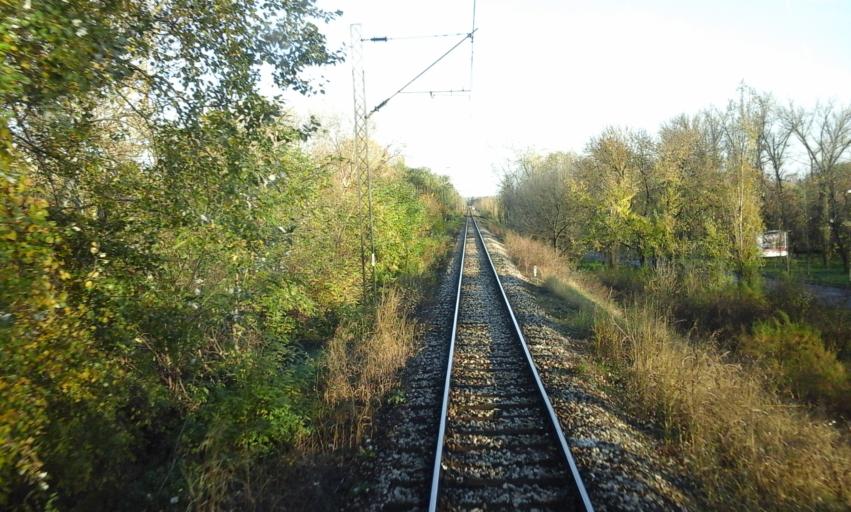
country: RS
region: Autonomna Pokrajina Vojvodina
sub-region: Juznobacki Okrug
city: Petrovaradin
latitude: 45.2592
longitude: 19.8663
